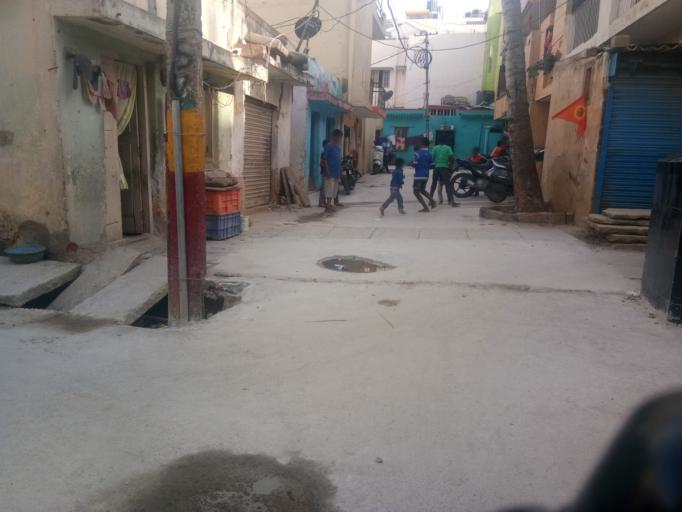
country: IN
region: Karnataka
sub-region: Bangalore Urban
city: Bangalore
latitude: 13.0119
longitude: 77.6275
